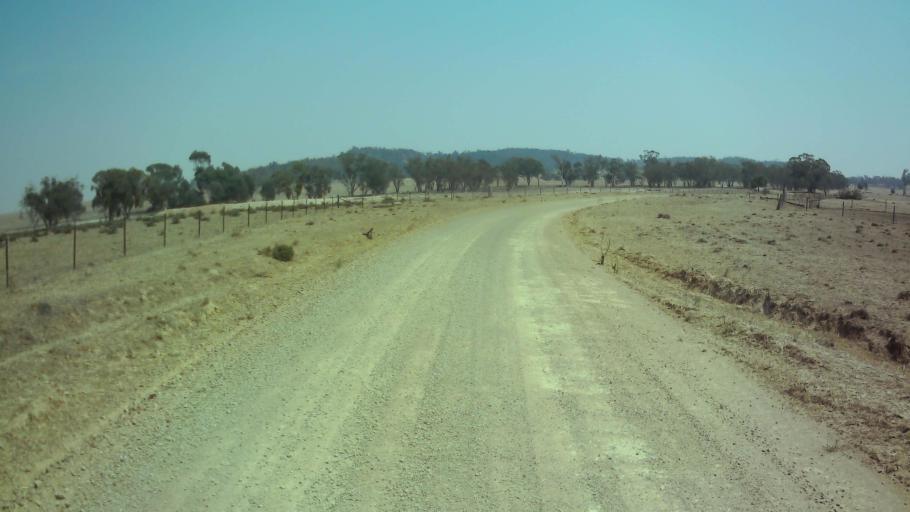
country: AU
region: New South Wales
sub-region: Weddin
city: Grenfell
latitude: -33.6764
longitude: 148.2760
